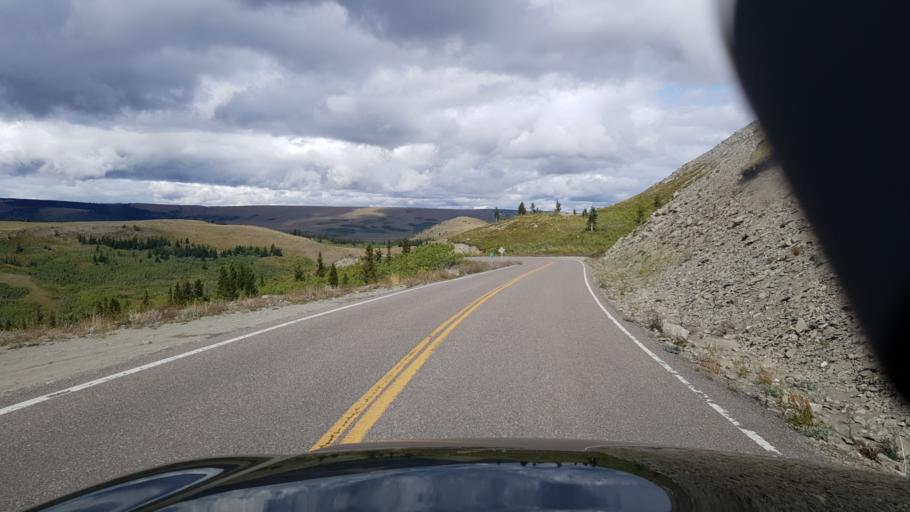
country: US
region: Montana
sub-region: Glacier County
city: South Browning
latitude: 48.5404
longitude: -113.3045
